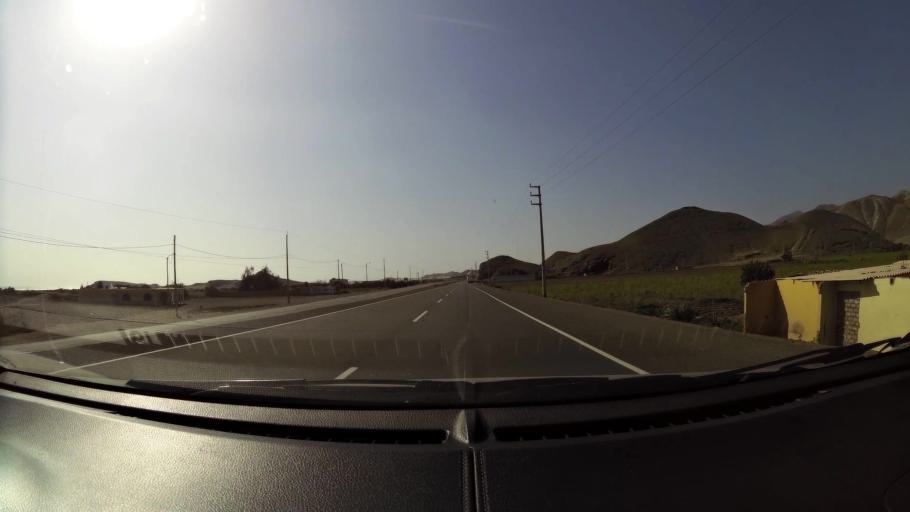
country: PE
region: Ancash
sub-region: Provincia de Huarmey
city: La Caleta Culebras
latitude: -9.9344
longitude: -78.2190
